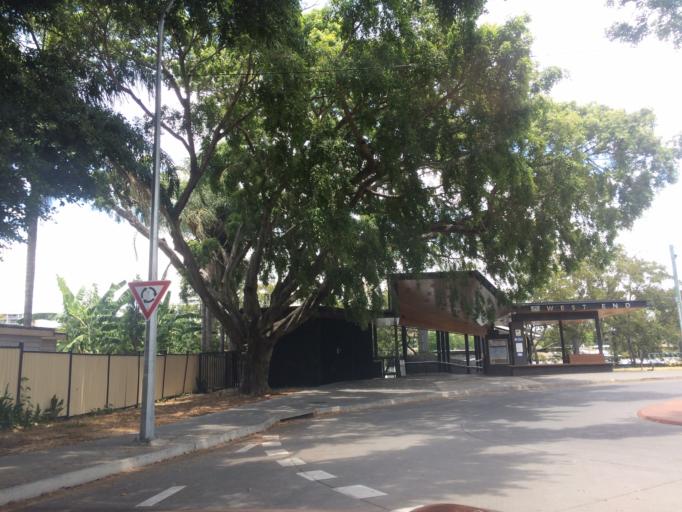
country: AU
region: Queensland
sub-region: Brisbane
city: Toowong
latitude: -27.4896
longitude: 153.0035
